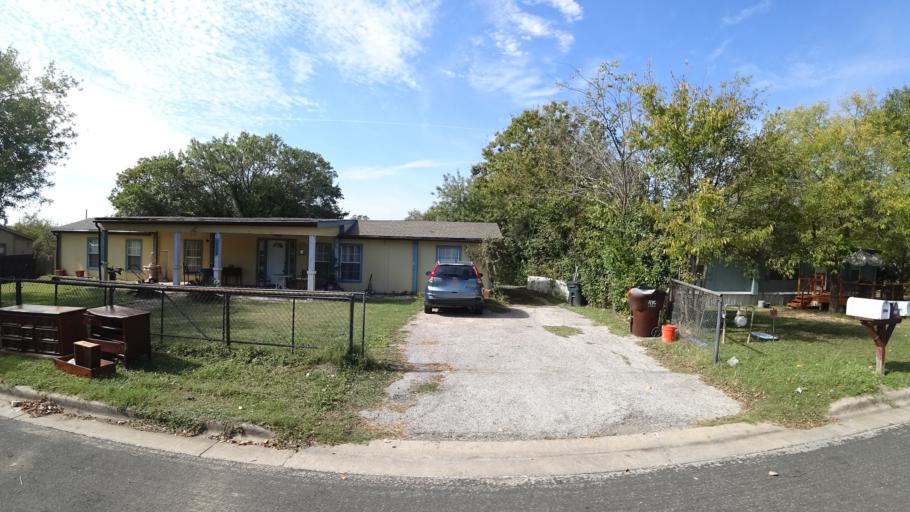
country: US
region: Texas
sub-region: Travis County
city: Pflugerville
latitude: 30.4105
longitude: -97.6317
